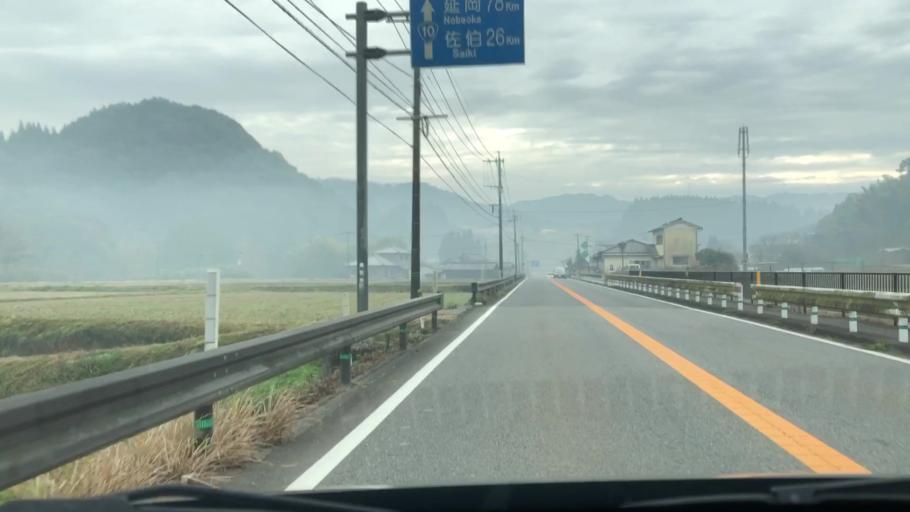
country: JP
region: Oita
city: Usuki
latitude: 33.0195
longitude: 131.6986
